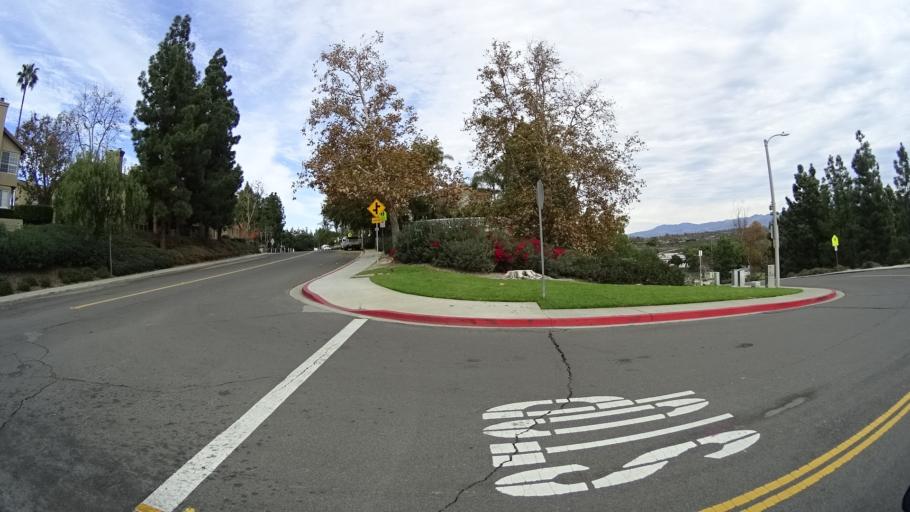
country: US
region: California
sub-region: Orange County
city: Aliso Viejo
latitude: 33.5671
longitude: -117.7196
